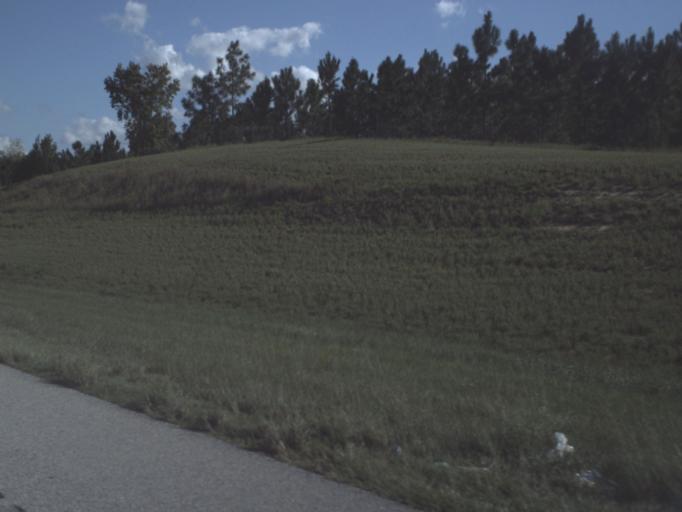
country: US
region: Florida
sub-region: Lake County
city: Minneola
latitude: 28.6110
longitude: -81.7303
